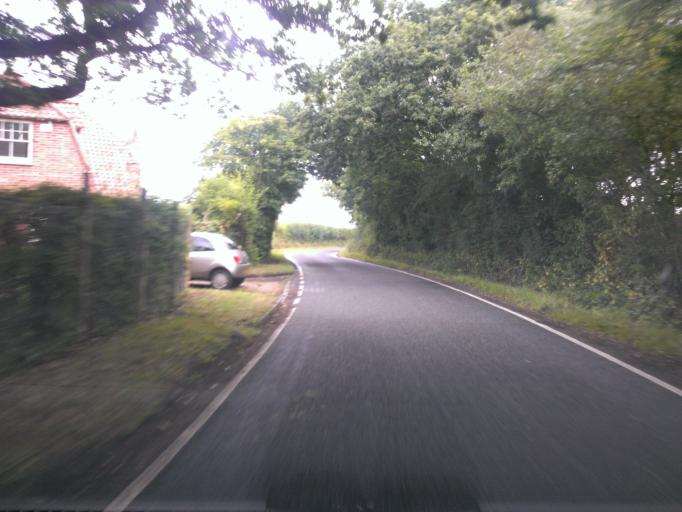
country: GB
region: England
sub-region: Essex
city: Wivenhoe
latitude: 51.8786
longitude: 0.9728
